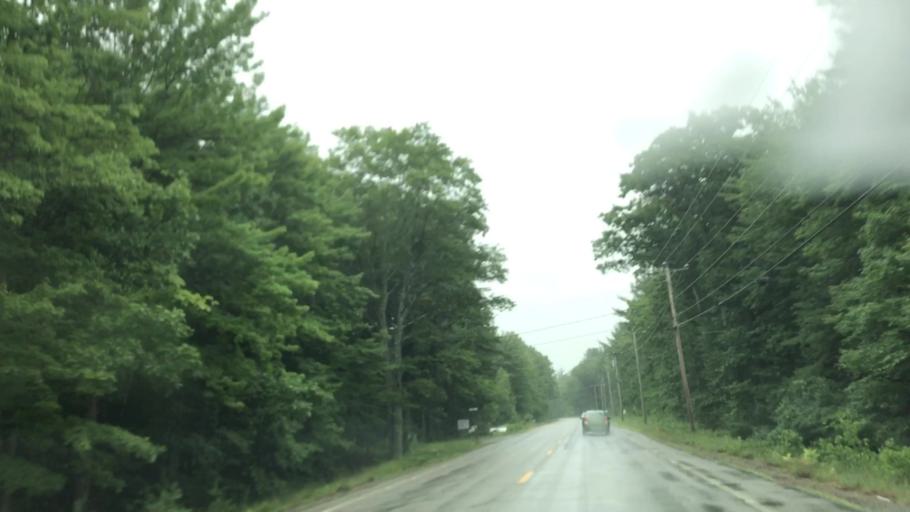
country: US
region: Maine
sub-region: York County
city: South Berwick
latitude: 43.2846
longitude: -70.8031
